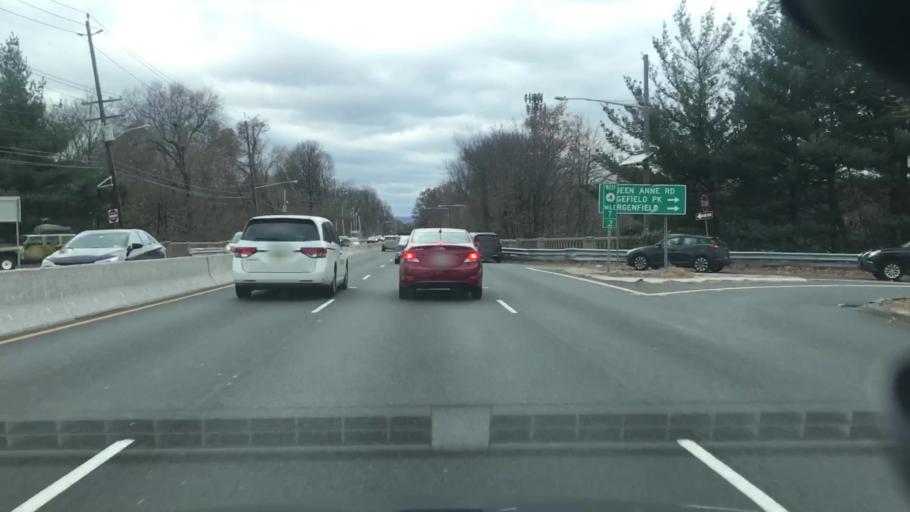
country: US
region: New Jersey
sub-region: Bergen County
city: Teaneck
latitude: 40.8930
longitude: -74.0109
